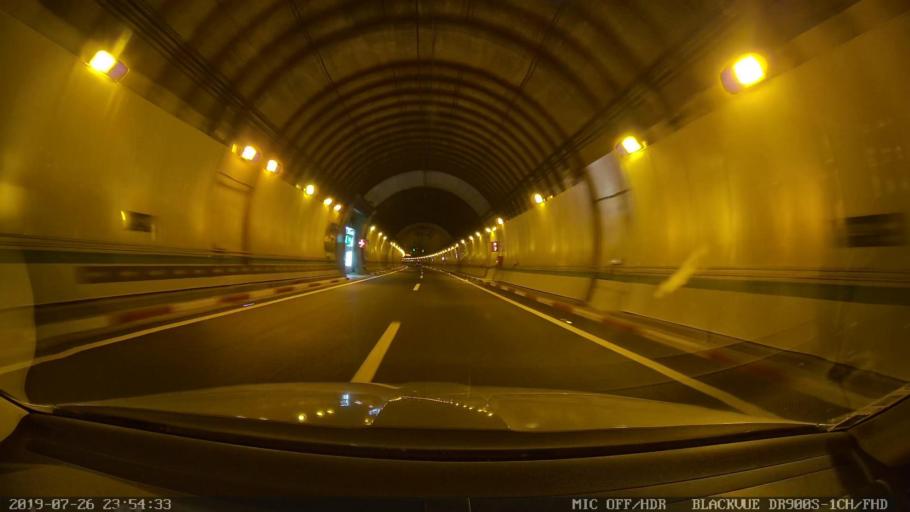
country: ES
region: Extremadura
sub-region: Provincia de Caceres
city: Romangordo
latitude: 39.6914
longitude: -5.7047
